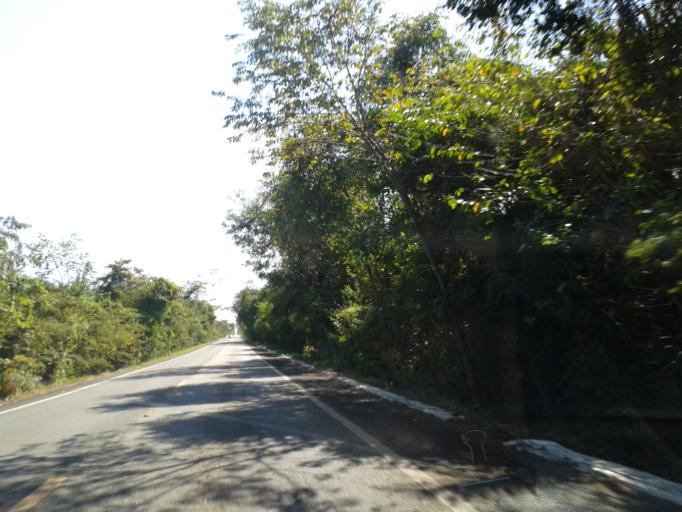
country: BR
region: Goias
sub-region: Crixas
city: Crixas
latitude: -14.0010
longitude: -50.3247
